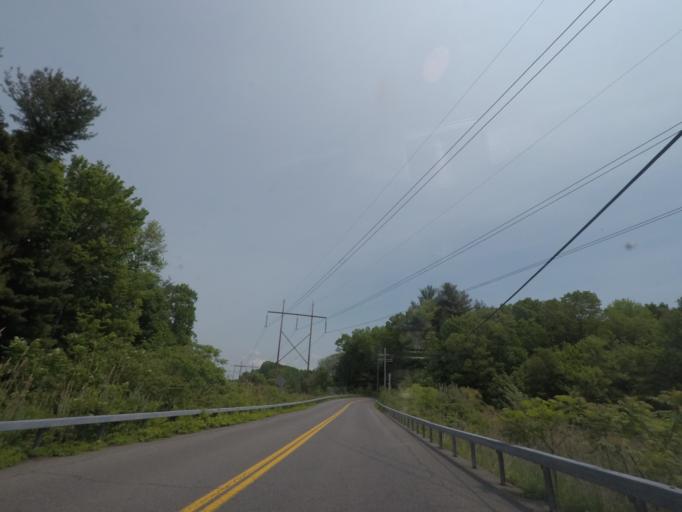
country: US
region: New York
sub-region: Columbia County
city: Niverville
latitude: 42.4824
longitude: -73.6985
